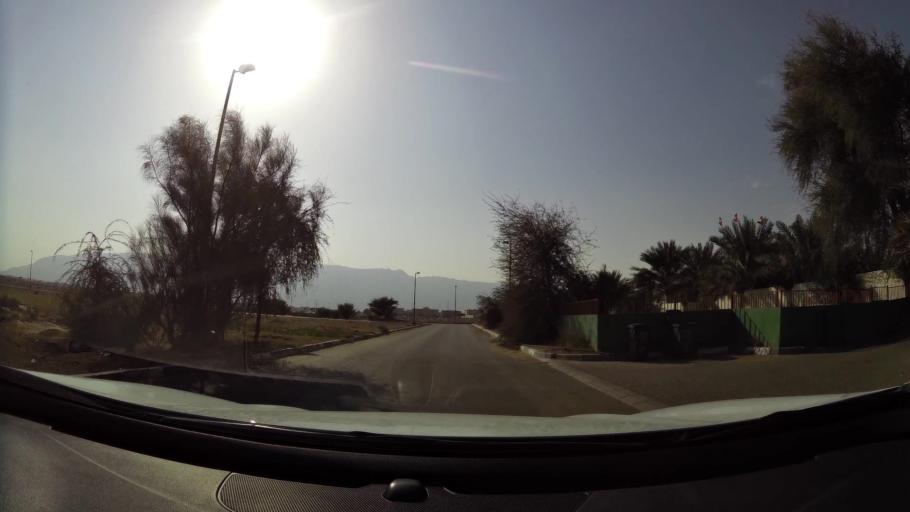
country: AE
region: Abu Dhabi
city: Al Ain
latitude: 24.0698
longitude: 55.8619
